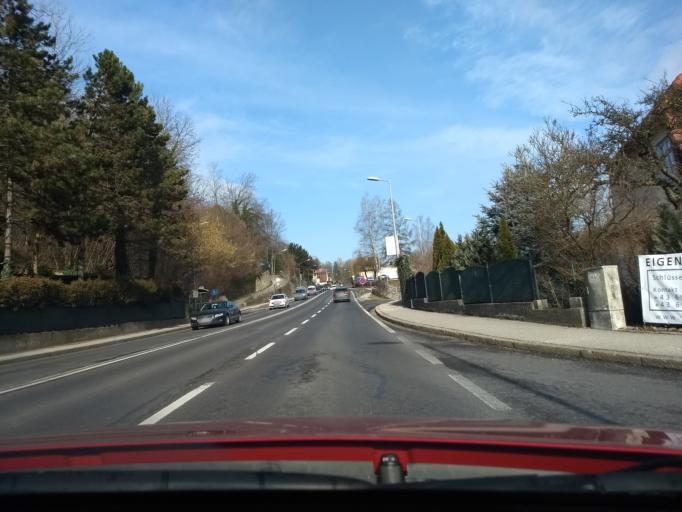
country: AT
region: Upper Austria
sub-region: Steyr Stadt
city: Steyr
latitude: 48.0458
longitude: 14.4277
